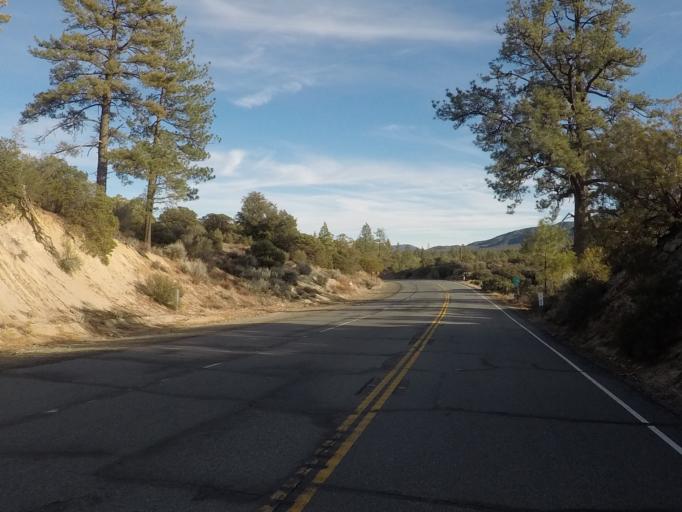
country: US
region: California
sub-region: Riverside County
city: Idyllwild
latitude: 33.6748
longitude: -116.6818
